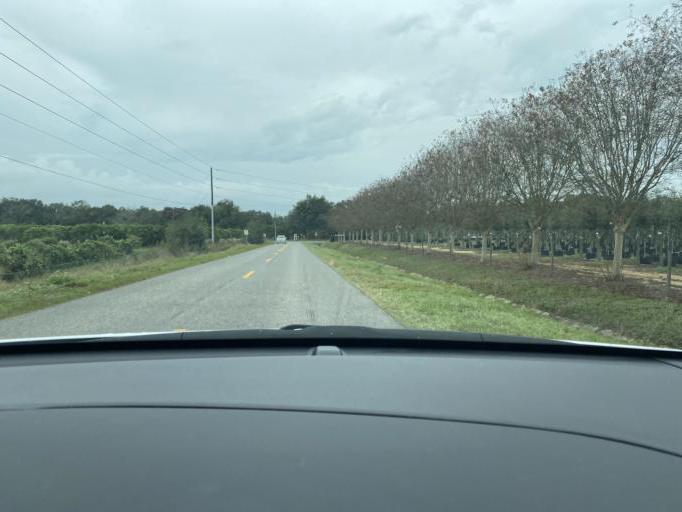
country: US
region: Florida
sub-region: Lake County
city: Groveland
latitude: 28.5876
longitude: -81.8498
